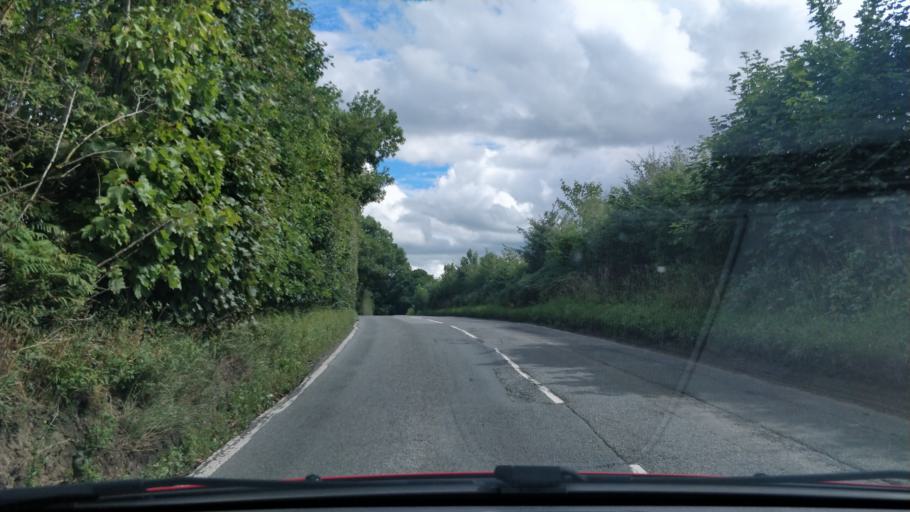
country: GB
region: Wales
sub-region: County of Flintshire
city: Hope
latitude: 53.1130
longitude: -3.0253
